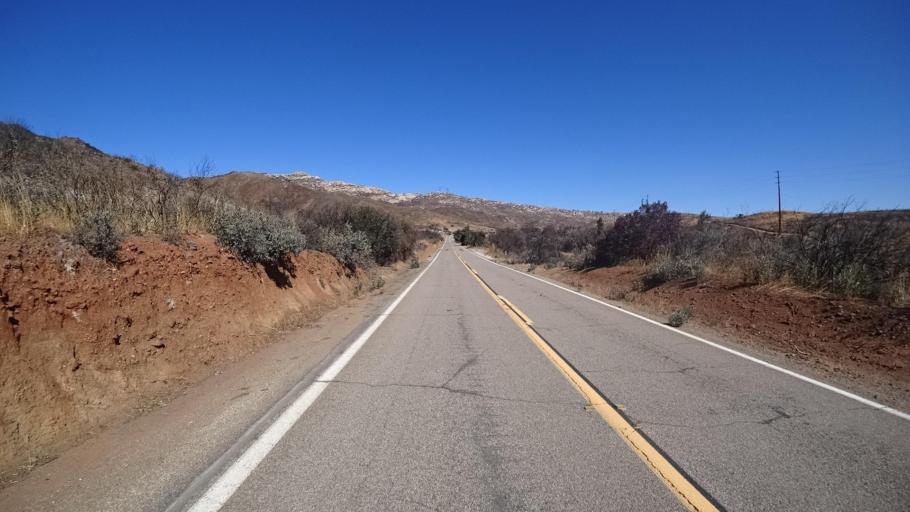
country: US
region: California
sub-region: San Diego County
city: Alpine
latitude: 32.7161
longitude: -116.7051
